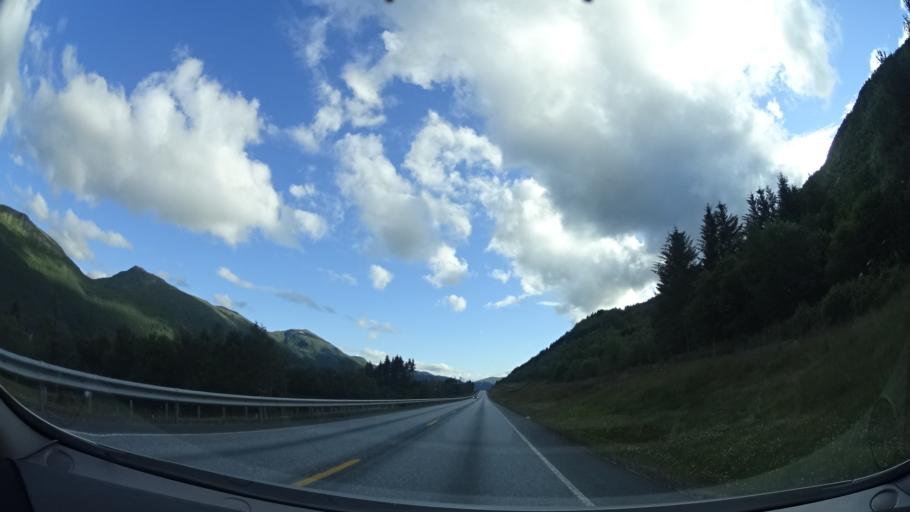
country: NO
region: More og Romsdal
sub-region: Gjemnes
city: Batnfjordsora
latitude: 62.9235
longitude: 7.7028
